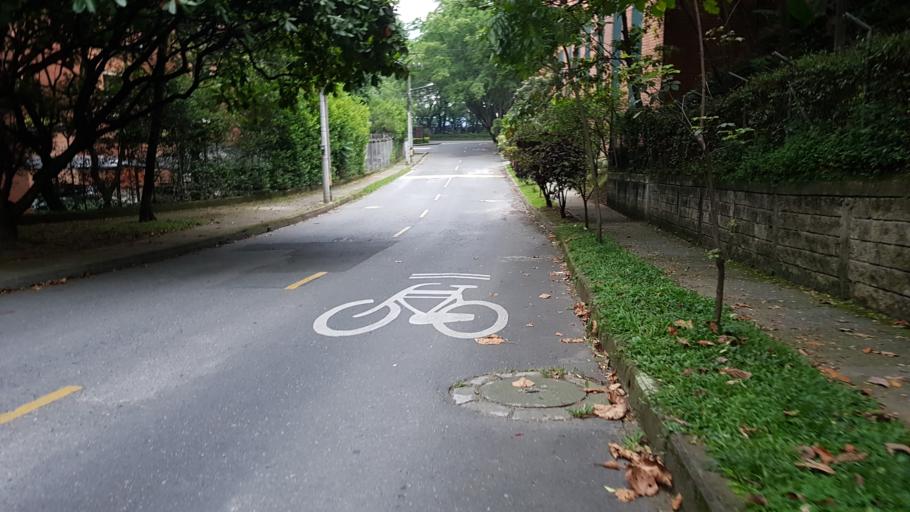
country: CO
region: Antioquia
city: Envigado
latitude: 6.1780
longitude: -75.5879
